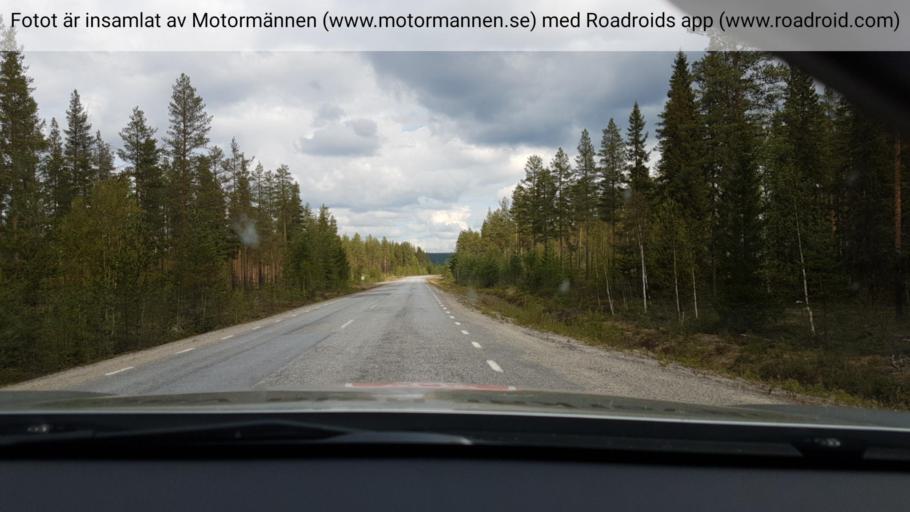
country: SE
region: Vaesternorrland
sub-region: OErnskoeldsviks Kommun
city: Bredbyn
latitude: 63.9541
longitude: 18.4837
